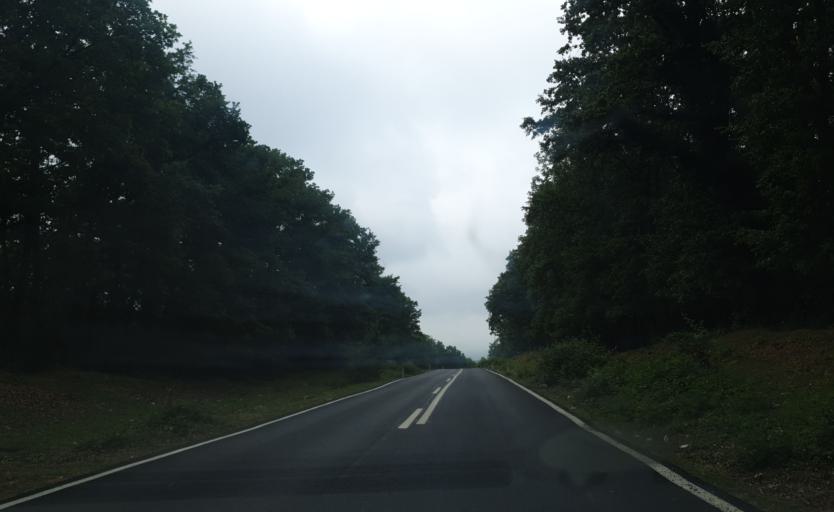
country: TR
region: Kirklareli
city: Salmydessus
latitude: 41.6029
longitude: 28.0867
